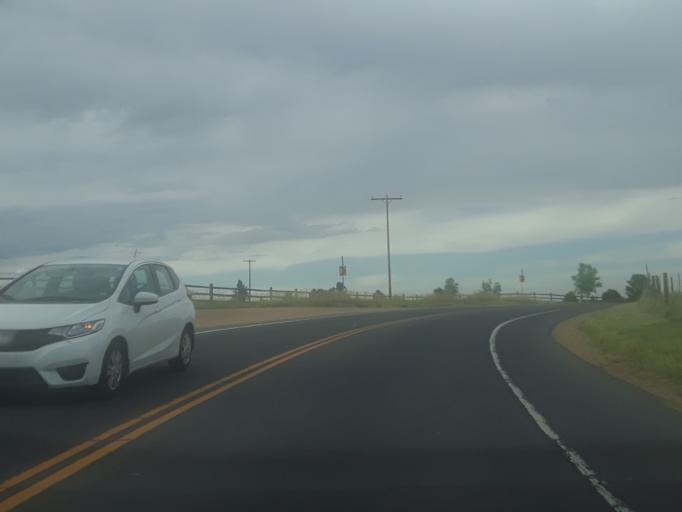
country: US
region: Colorado
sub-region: Boulder County
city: Superior
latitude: 39.9591
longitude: -105.2234
